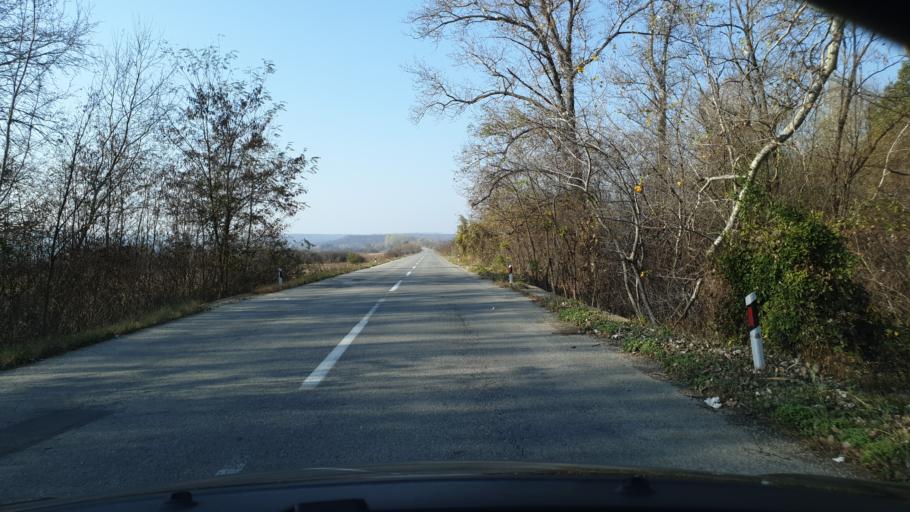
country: BG
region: Vidin
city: Bregovo
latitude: 44.1564
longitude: 22.6158
